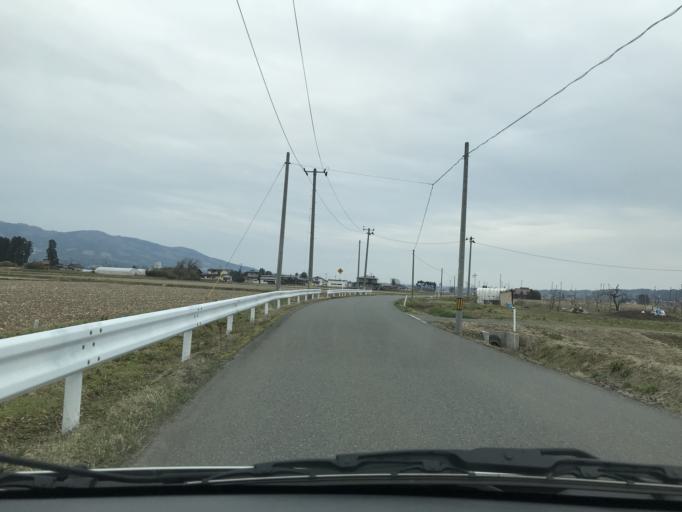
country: JP
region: Iwate
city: Mizusawa
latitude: 39.0821
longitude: 141.1441
